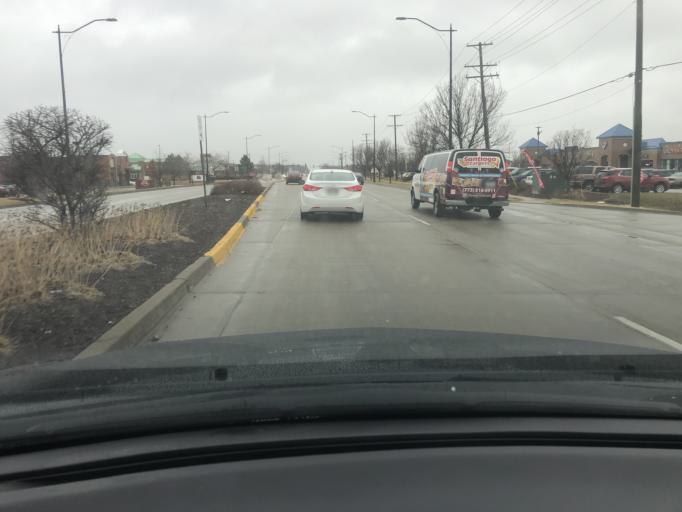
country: US
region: Illinois
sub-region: Will County
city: Shorewood
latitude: 41.5394
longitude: -88.1994
